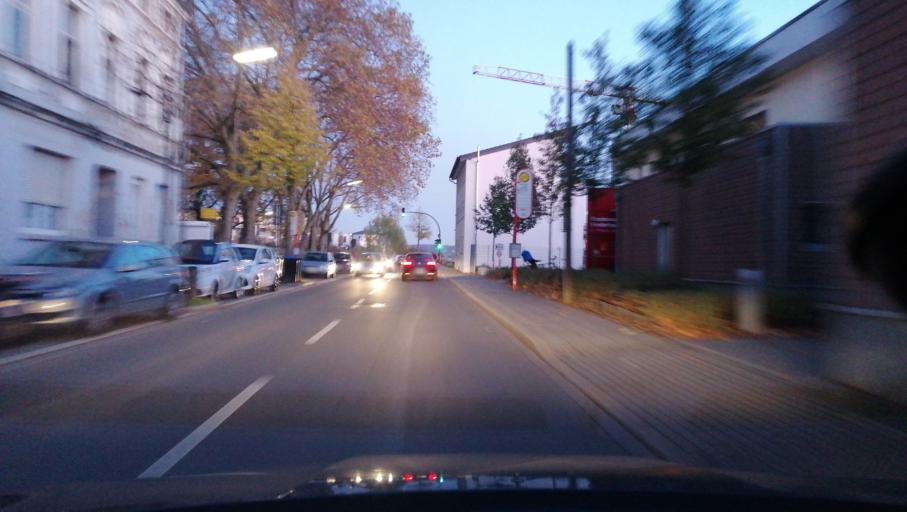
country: DE
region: North Rhine-Westphalia
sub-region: Regierungsbezirk Arnsberg
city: Dortmund
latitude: 51.4934
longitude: 7.5060
